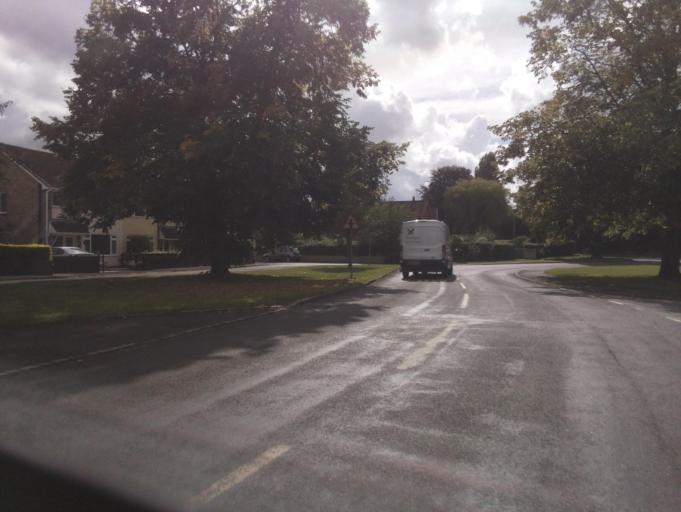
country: GB
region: England
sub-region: Staffordshire
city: Barlaston
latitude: 52.9420
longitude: -2.1713
